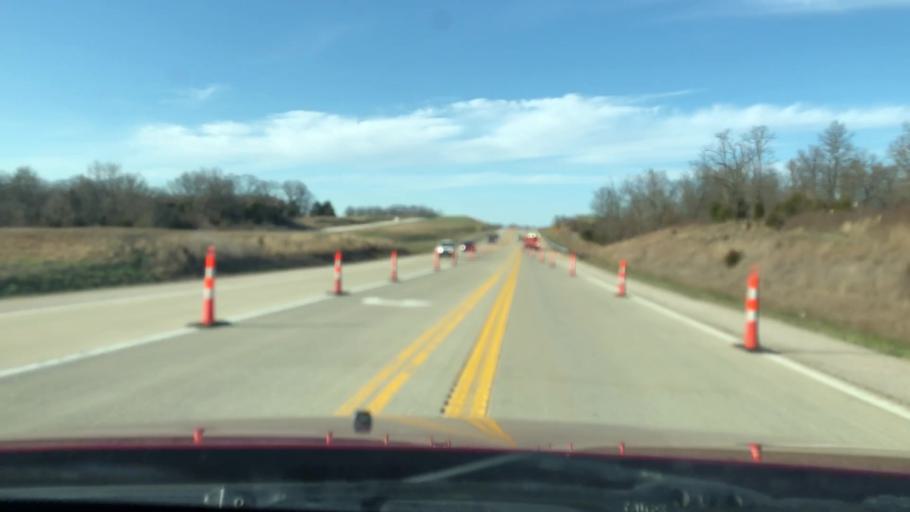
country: US
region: Missouri
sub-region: Camden County
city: Camdenton
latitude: 37.9529
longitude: -92.7153
